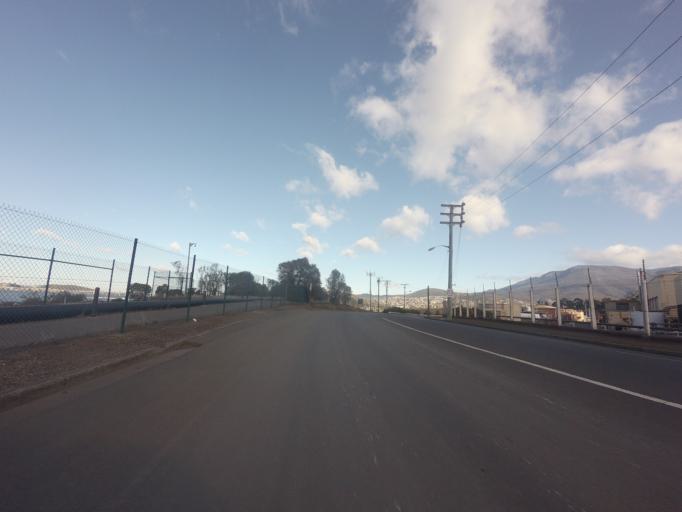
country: AU
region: Tasmania
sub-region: Glenorchy
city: Lutana
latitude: -42.8359
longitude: 147.3220
